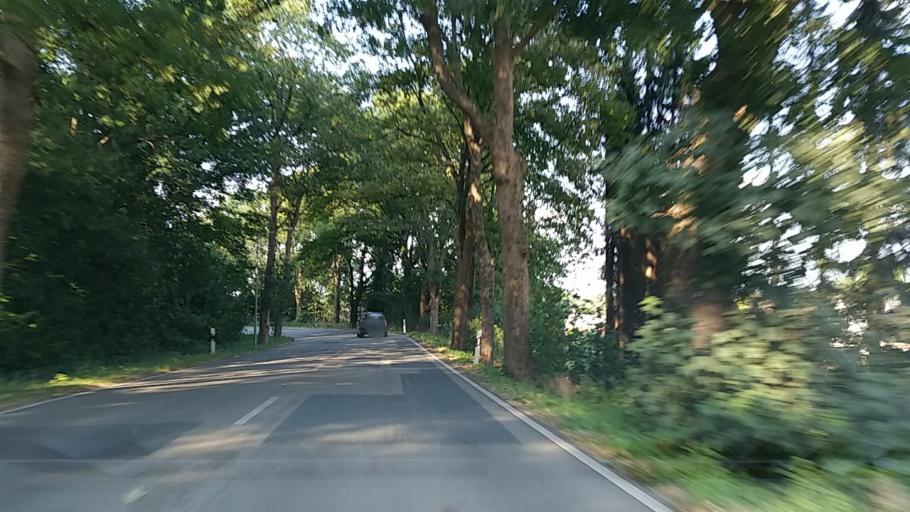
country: DE
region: Lower Saxony
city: Neu Wulmstorf
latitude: 53.4568
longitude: 9.8006
